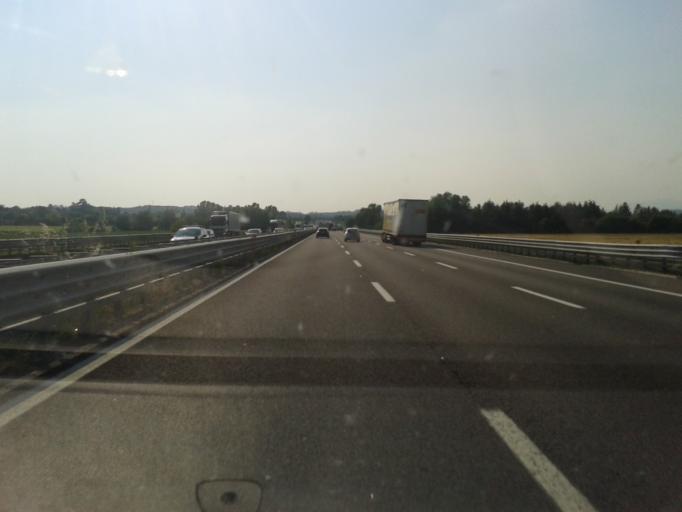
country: IT
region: Lombardy
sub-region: Provincia di Brescia
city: Desenzano del Garda
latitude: 45.4417
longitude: 10.5604
